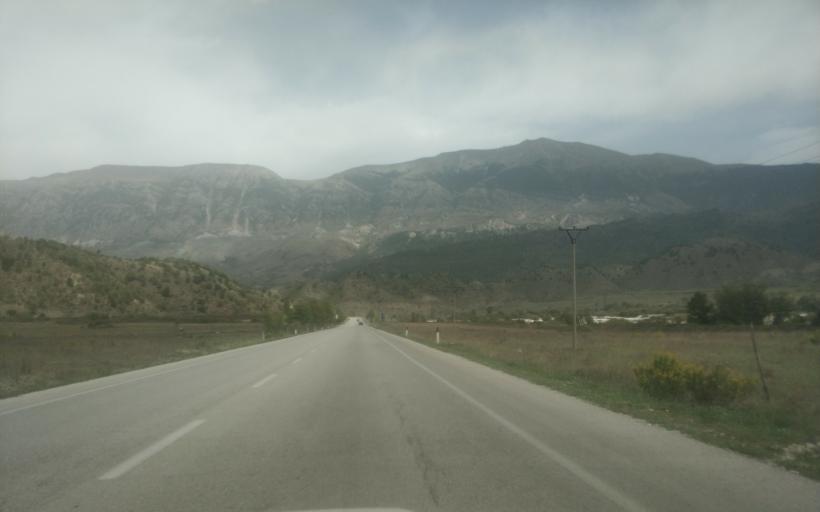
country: AL
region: Gjirokaster
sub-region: Rrethi i Gjirokastres
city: Picar
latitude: 40.1974
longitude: 20.0848
